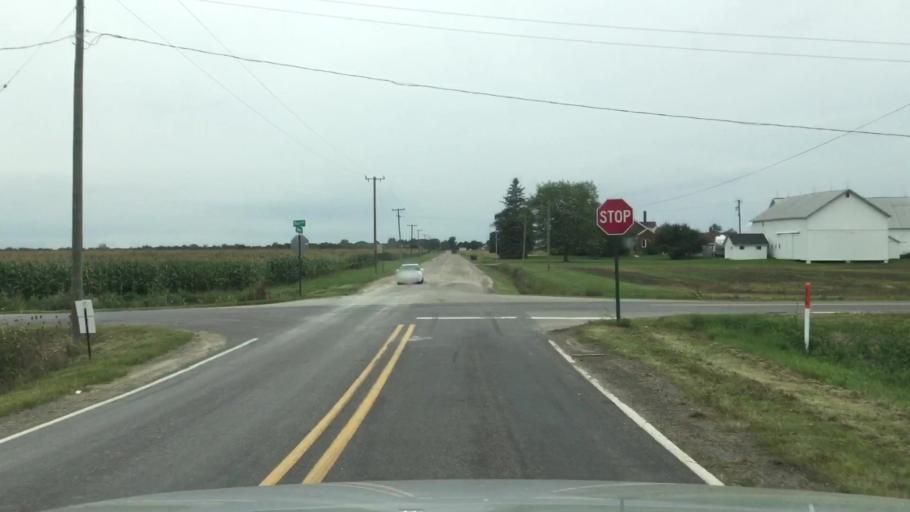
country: US
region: Michigan
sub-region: Washtenaw County
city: Milan
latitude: 42.1131
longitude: -83.6957
